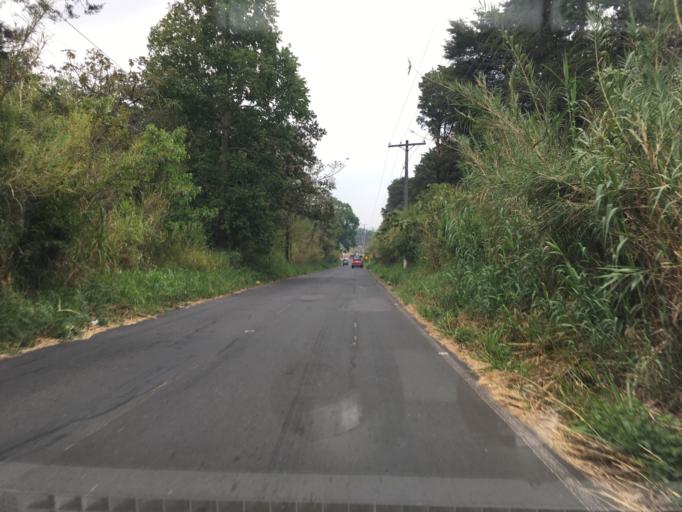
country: GT
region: Guatemala
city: Fraijanes
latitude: 14.3949
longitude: -90.4719
